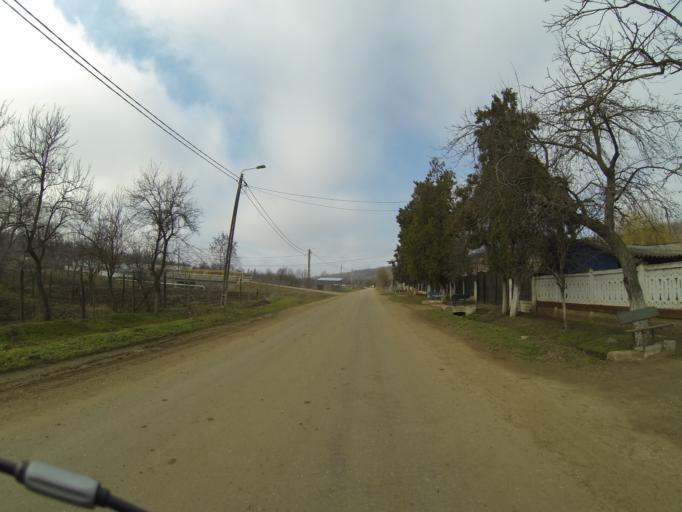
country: RO
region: Mehedinti
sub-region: Comuna Poroina Mare
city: Poroina Mare
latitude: 44.4928
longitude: 22.9991
